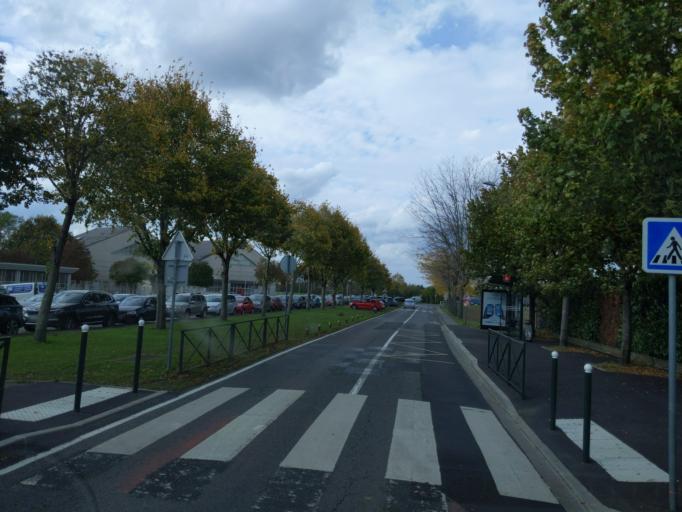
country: FR
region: Ile-de-France
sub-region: Departement des Yvelines
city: Rambouillet
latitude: 48.6481
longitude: 1.8487
